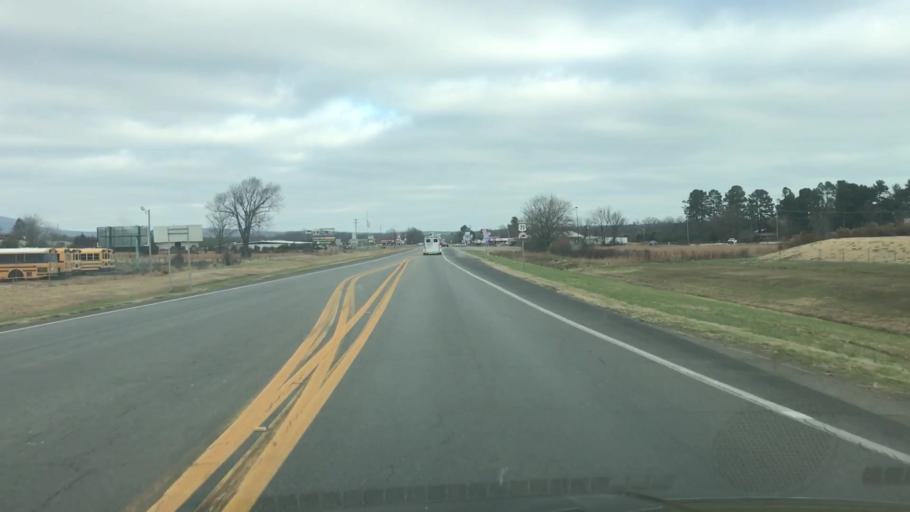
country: US
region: Arkansas
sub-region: Scott County
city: Waldron
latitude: 34.8973
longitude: -94.1075
